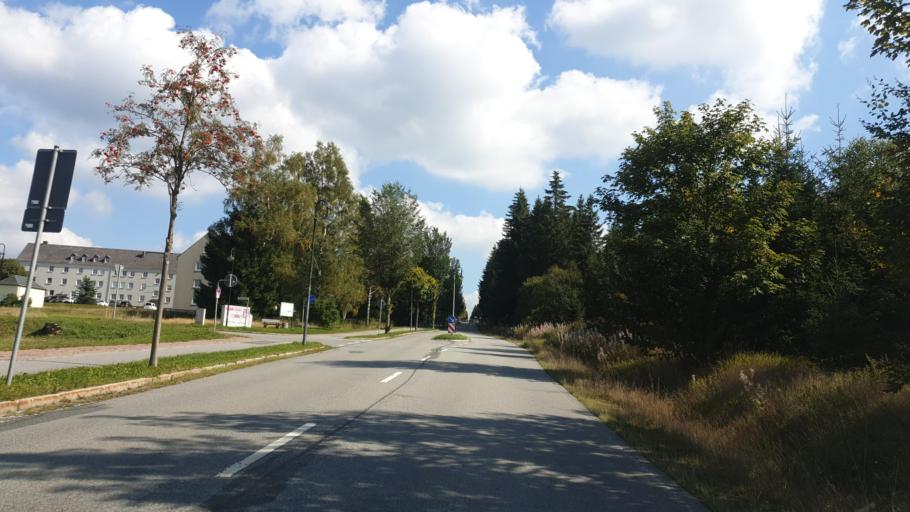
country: DE
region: Saxony
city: Johanngeorgenstadt
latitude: 50.4413
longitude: 12.6877
